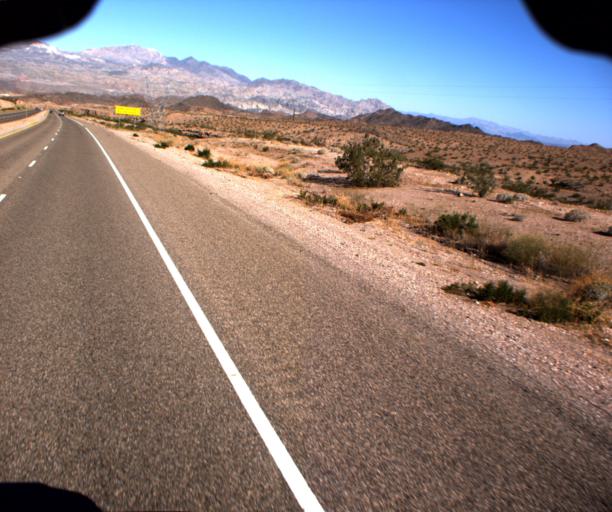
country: US
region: Nevada
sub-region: Clark County
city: Laughlin
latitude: 35.1881
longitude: -114.5075
